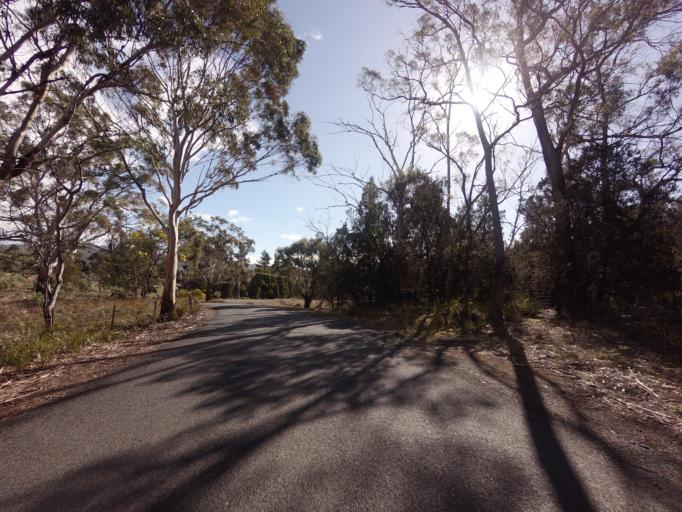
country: AU
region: Tasmania
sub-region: Sorell
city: Sorell
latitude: -42.3605
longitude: 147.9434
